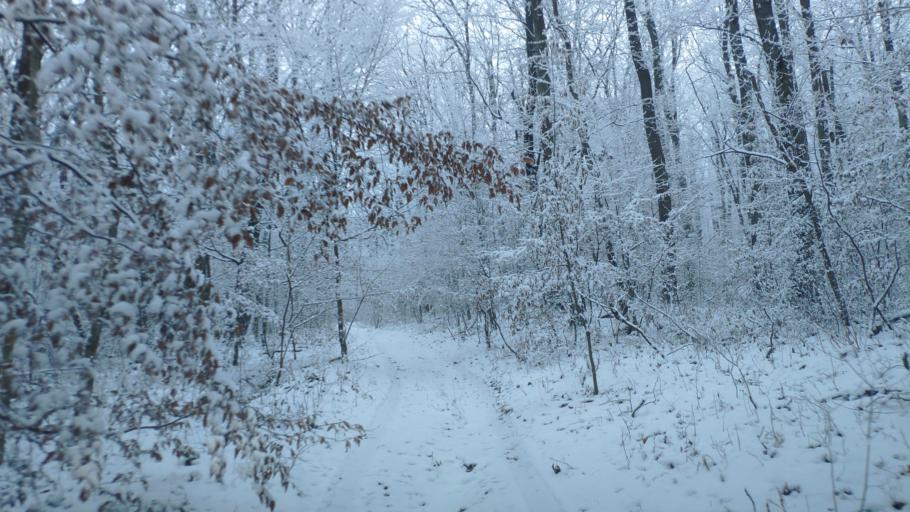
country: SK
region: Kosicky
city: Kosice
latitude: 48.6459
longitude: 21.1796
